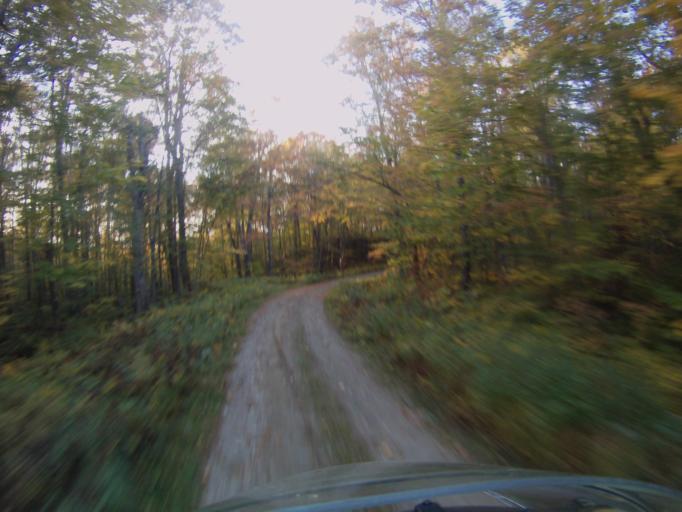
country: US
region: Vermont
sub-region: Addison County
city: Bristol
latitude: 44.0831
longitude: -72.9393
